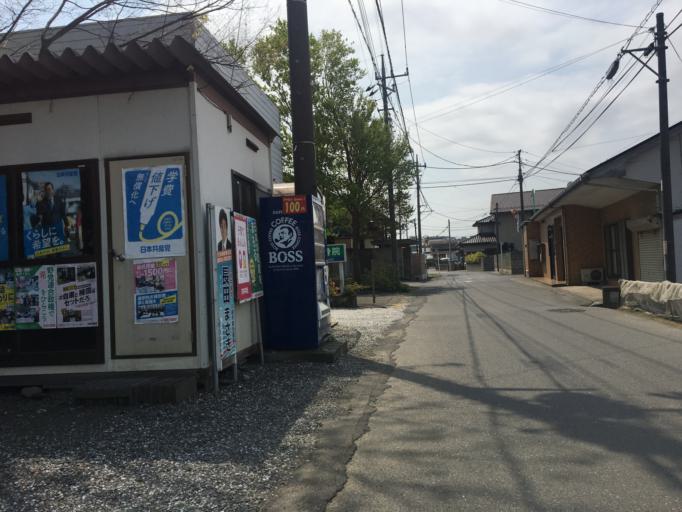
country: JP
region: Saitama
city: Kamifukuoka
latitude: 35.8882
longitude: 139.5260
